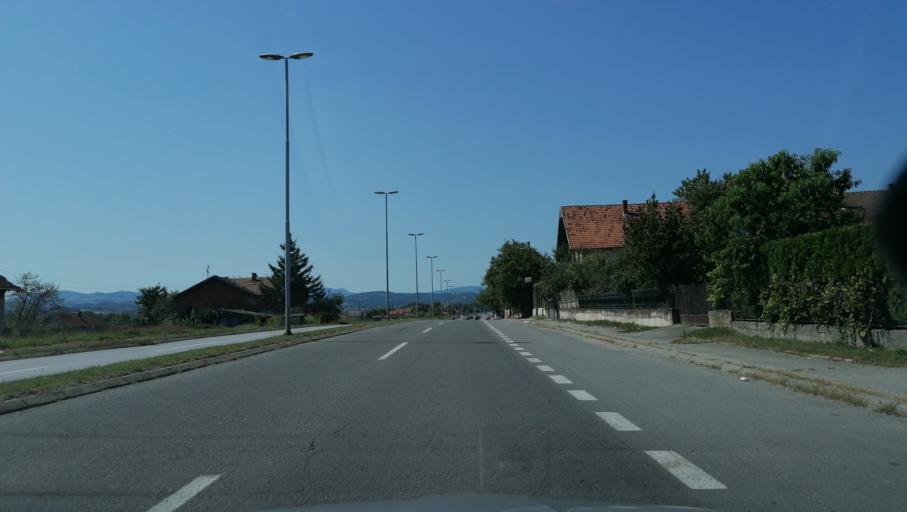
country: RS
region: Central Serbia
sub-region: Kolubarski Okrug
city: Valjevo
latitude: 44.2906
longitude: 19.9551
